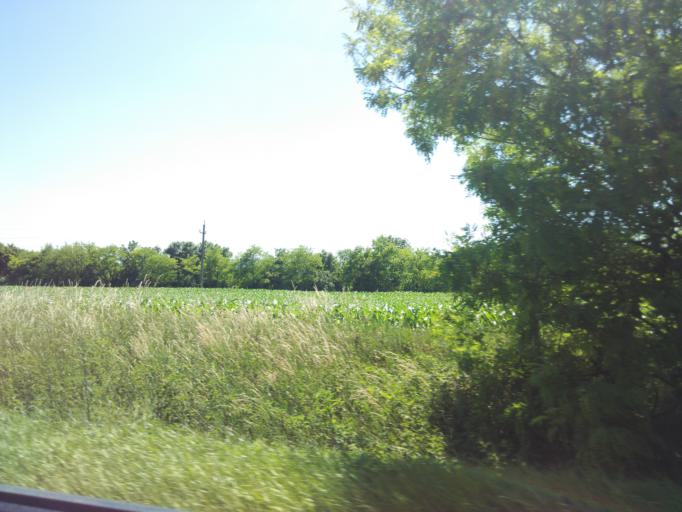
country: HU
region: Fejer
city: Kincsesbanya
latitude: 47.2801
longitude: 18.3159
